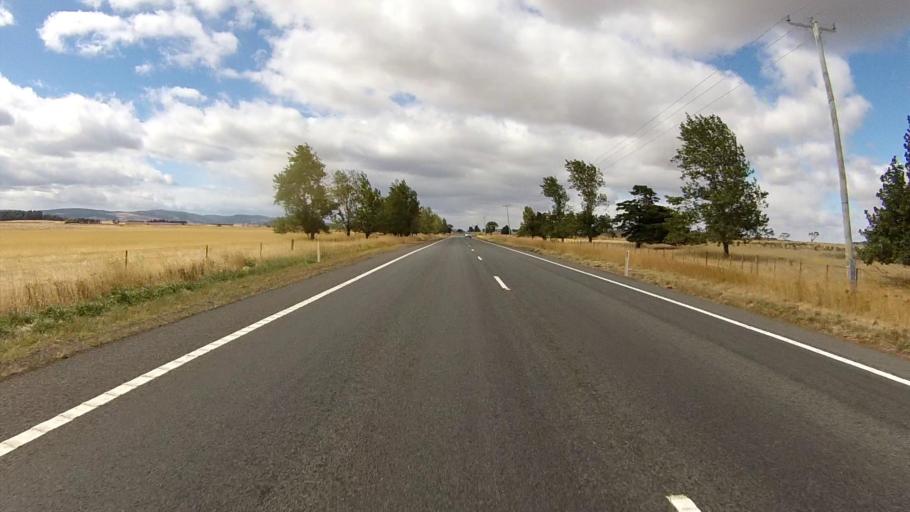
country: AU
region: Tasmania
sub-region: Northern Midlands
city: Evandale
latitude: -41.8886
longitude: 147.4693
